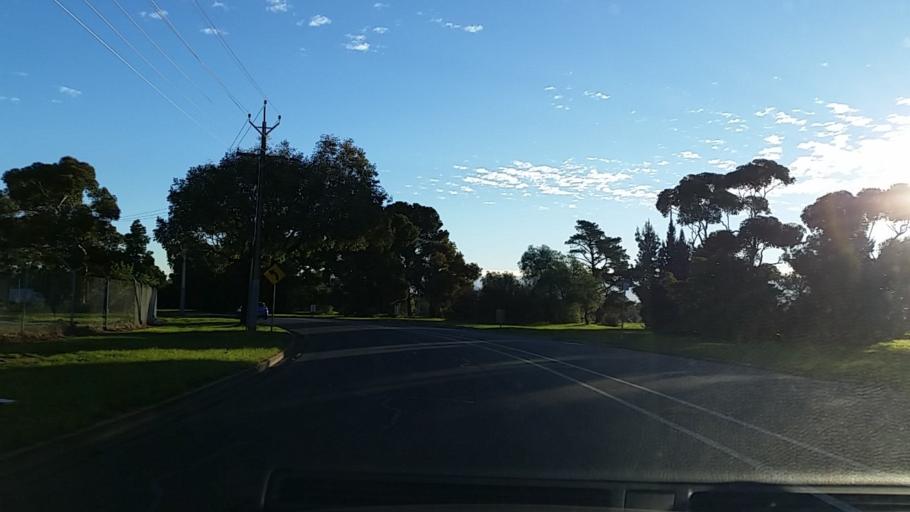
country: AU
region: South Australia
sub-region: Salisbury
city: Elizabeth
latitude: -34.7365
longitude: 138.6537
